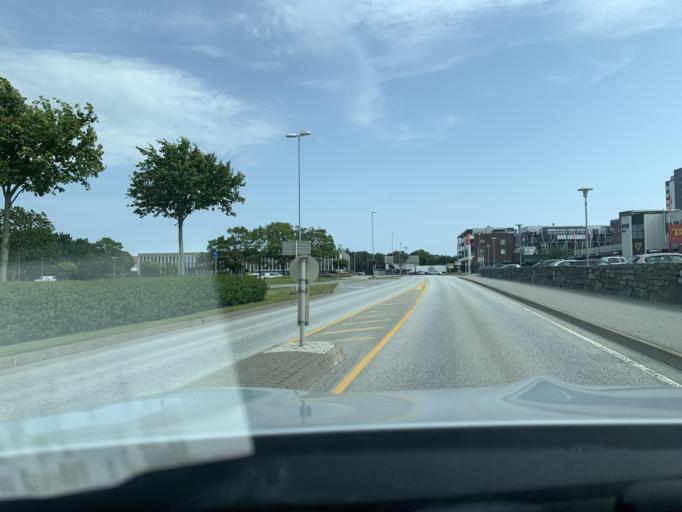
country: NO
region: Rogaland
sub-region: Klepp
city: Kleppe
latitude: 58.7774
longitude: 5.6269
